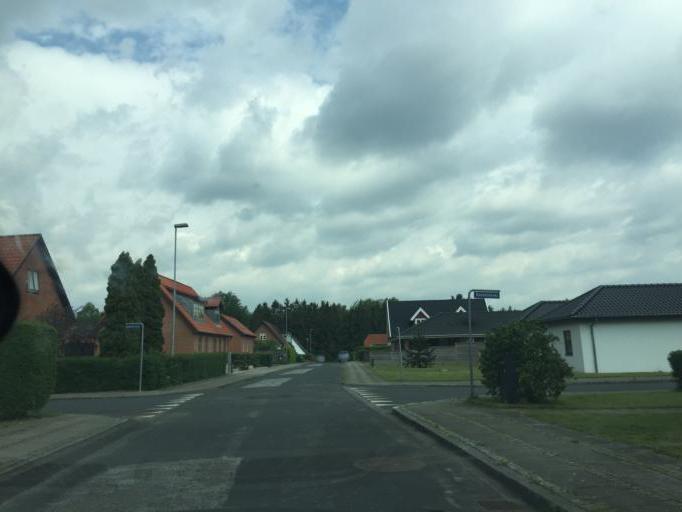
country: DK
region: South Denmark
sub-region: Odense Kommune
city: Odense
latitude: 55.3805
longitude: 10.3529
